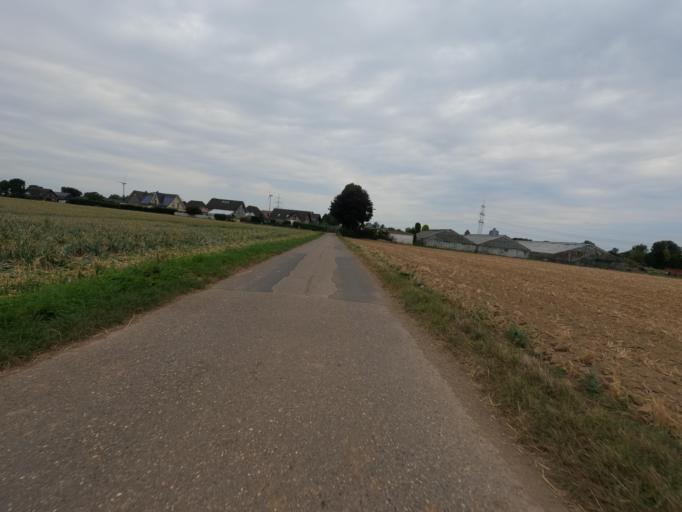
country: DE
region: North Rhine-Westphalia
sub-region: Regierungsbezirk Koln
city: Aldenhoven
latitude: 50.9334
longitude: 6.2978
